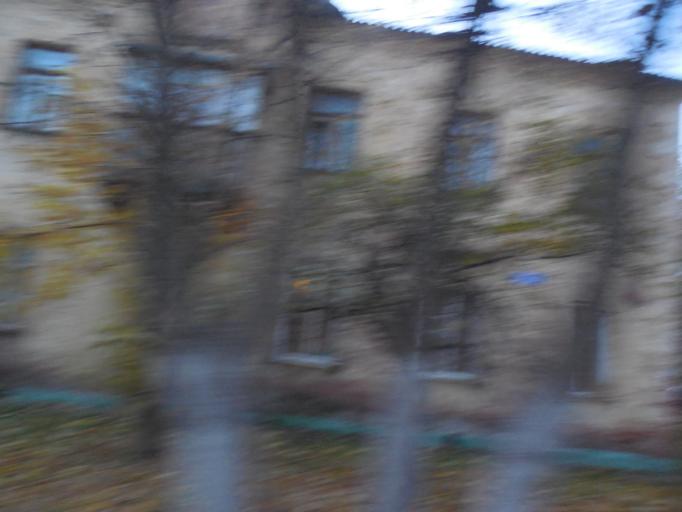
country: RU
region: Moskovskaya
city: Shcherbinka
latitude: 55.5129
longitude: 37.5678
